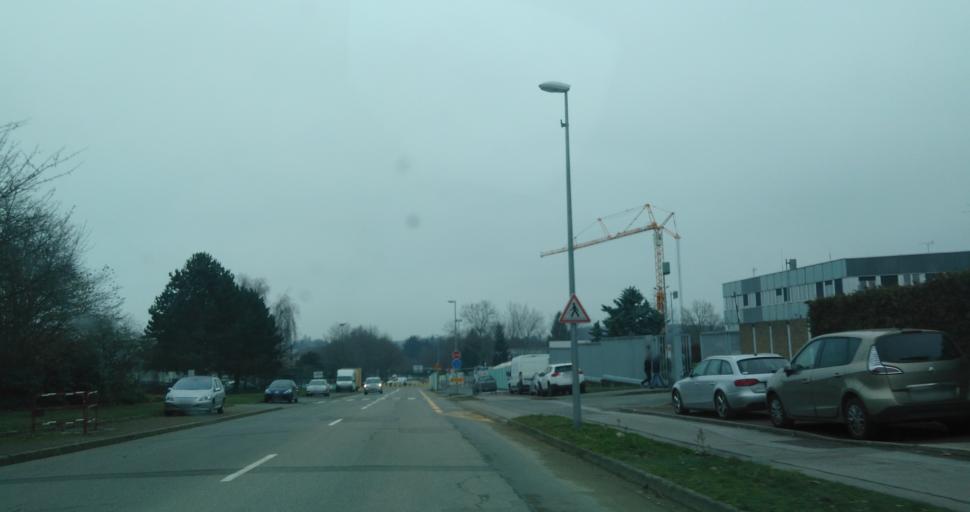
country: FR
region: Brittany
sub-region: Departement d'Ille-et-Vilaine
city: Cesson-Sevigne
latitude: 48.1257
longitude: -1.6281
